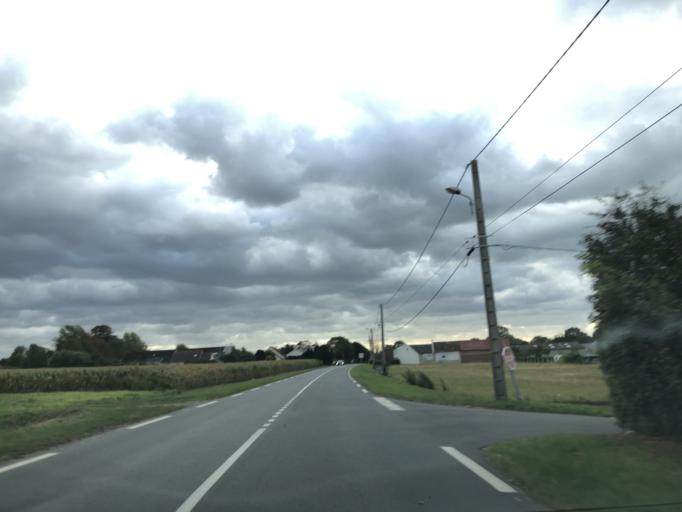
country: FR
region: Picardie
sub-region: Departement de la Somme
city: Cayeux-sur-Mer
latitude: 50.1427
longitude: 1.5295
